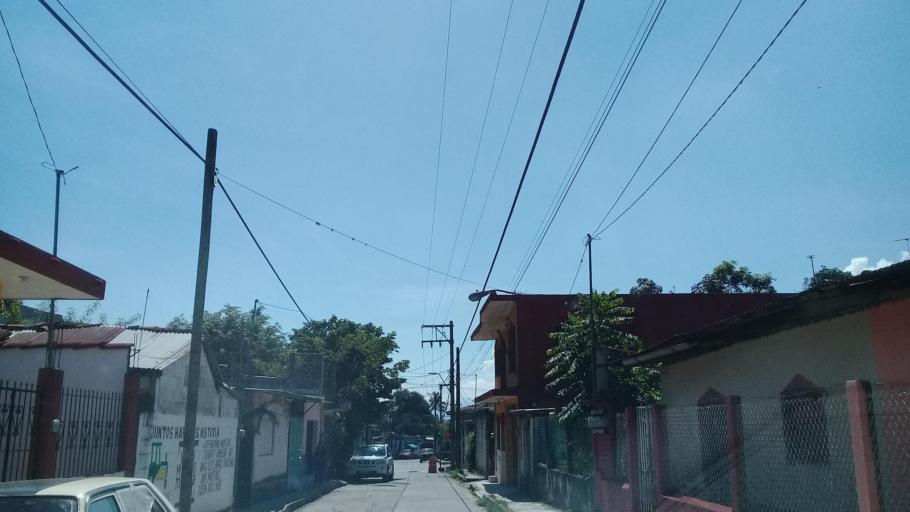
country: MX
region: Veracruz
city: Amatlan de los Reyes
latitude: 18.8485
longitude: -96.9163
